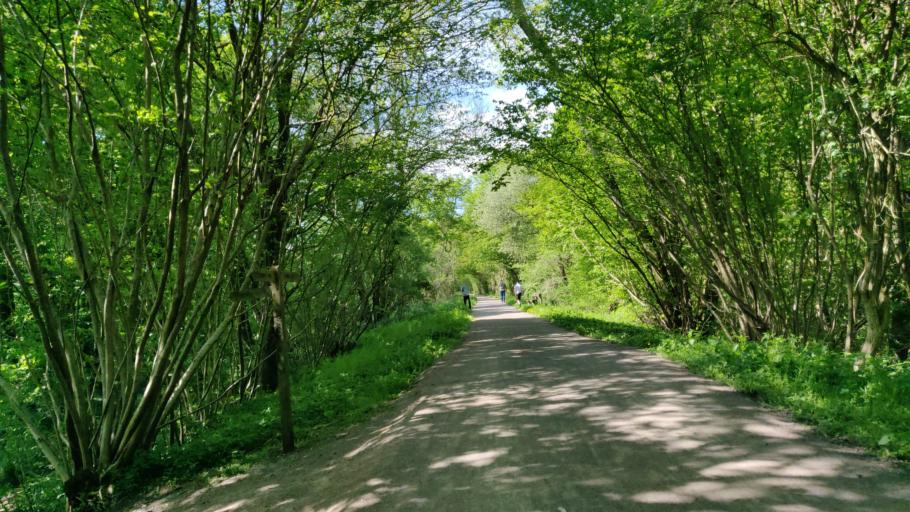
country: GB
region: England
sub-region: West Sussex
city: Rudgwick
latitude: 51.0816
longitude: -0.4360
